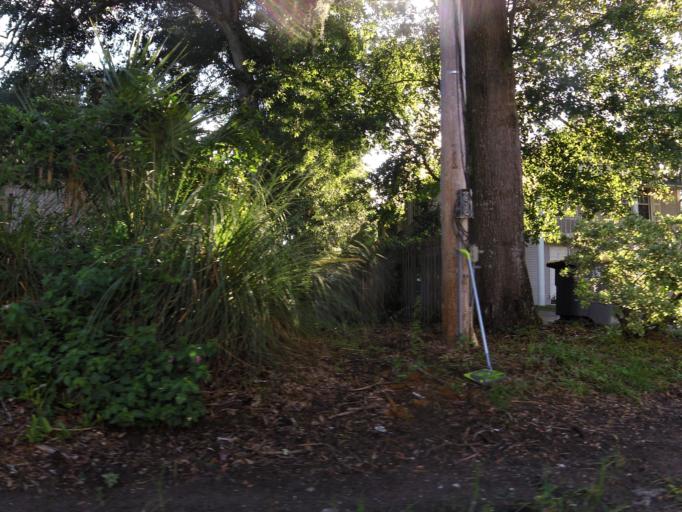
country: US
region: Florida
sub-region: Duval County
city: Jacksonville
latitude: 30.3017
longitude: -81.6299
